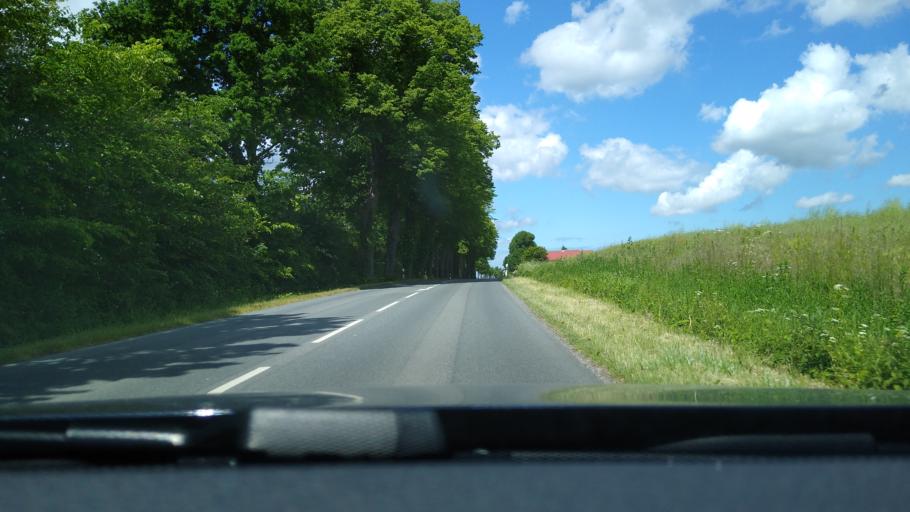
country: DE
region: Schleswig-Holstein
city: Riepsdorf
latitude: 54.1987
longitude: 10.9724
